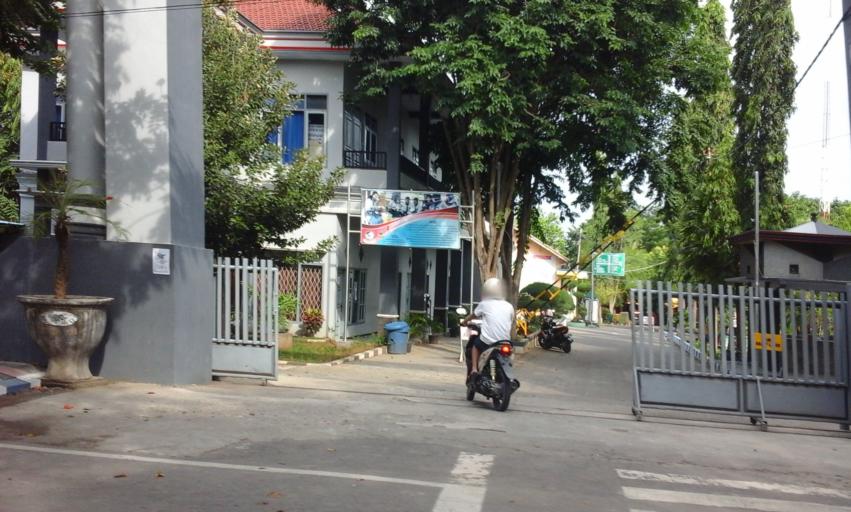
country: ID
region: East Java
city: Cungking
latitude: -8.2119
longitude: 114.3504
